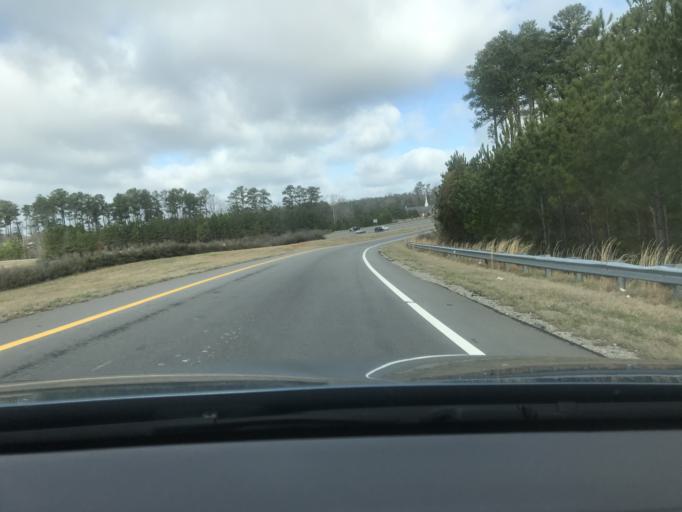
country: US
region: North Carolina
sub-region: Lee County
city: Sanford
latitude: 35.5126
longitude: -79.1860
